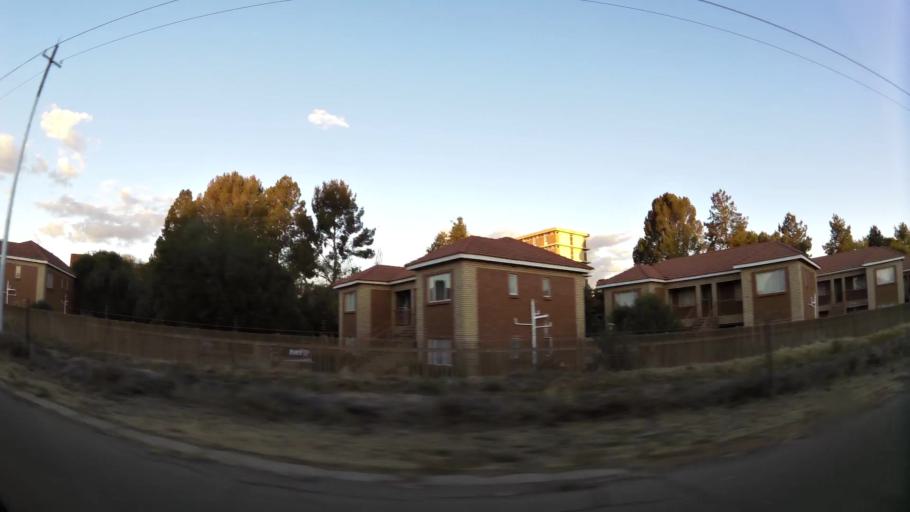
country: ZA
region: North-West
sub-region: Dr Kenneth Kaunda District Municipality
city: Potchefstroom
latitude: -26.6880
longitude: 27.0876
